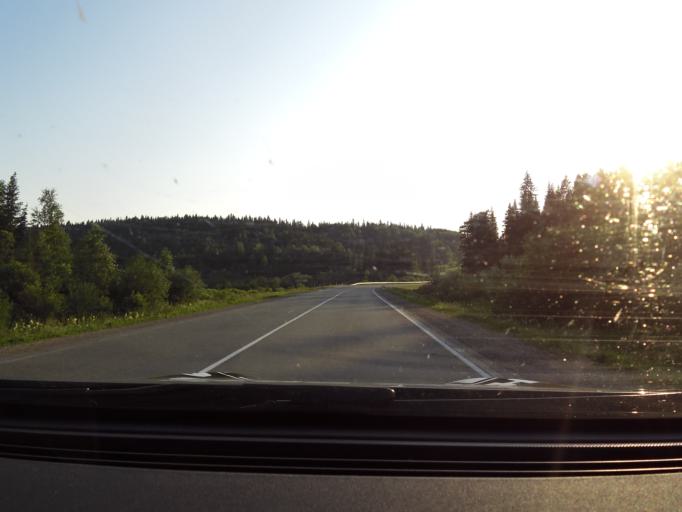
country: RU
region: Sverdlovsk
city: Mikhaylovsk
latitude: 56.5104
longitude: 59.1688
